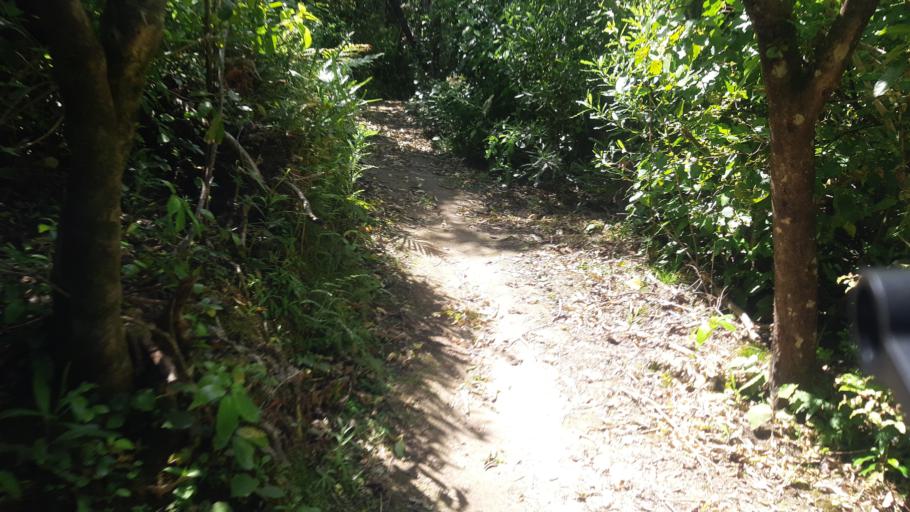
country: NZ
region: Marlborough
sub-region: Marlborough District
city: Picton
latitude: -41.2701
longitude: 174.0251
